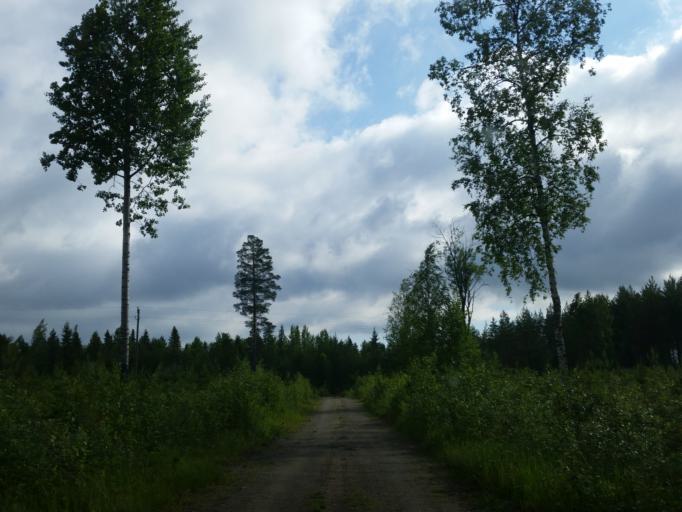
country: FI
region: Northern Savo
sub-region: Sisae-Savo
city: Tervo
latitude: 63.0727
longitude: 26.5999
